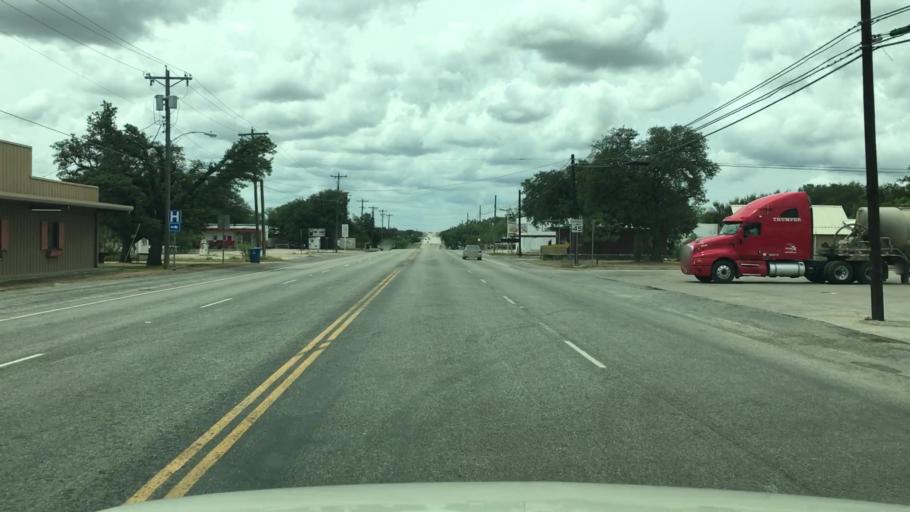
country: US
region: Texas
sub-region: Concho County
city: Eden
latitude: 31.2164
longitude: -99.8469
